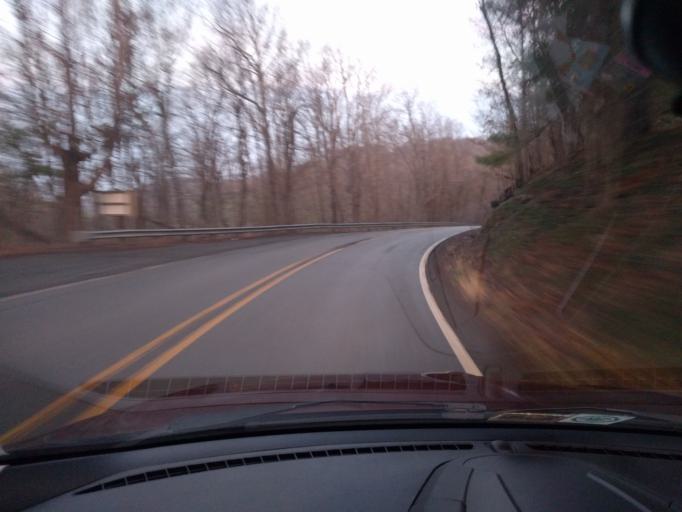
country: US
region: West Virginia
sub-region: Greenbrier County
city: Rainelle
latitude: 37.9943
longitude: -80.8668
